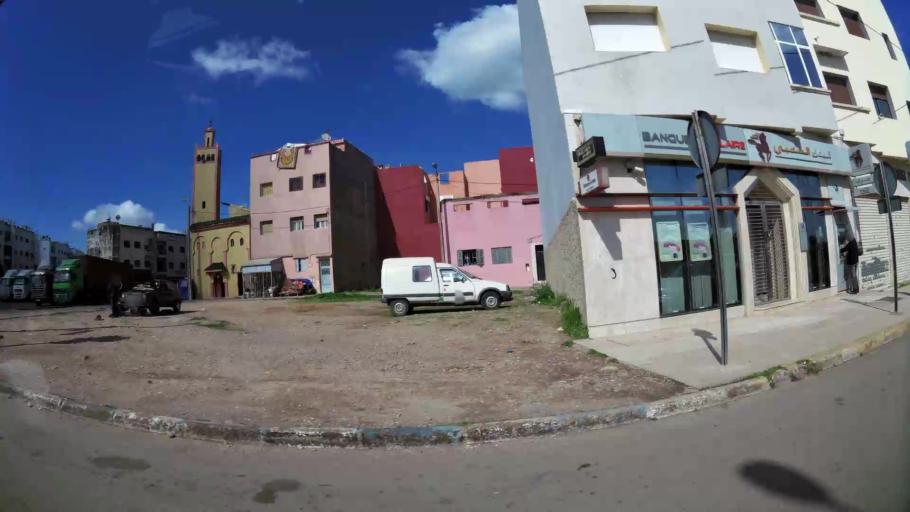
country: MA
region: Grand Casablanca
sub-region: Mediouna
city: Mediouna
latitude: 33.4558
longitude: -7.5168
